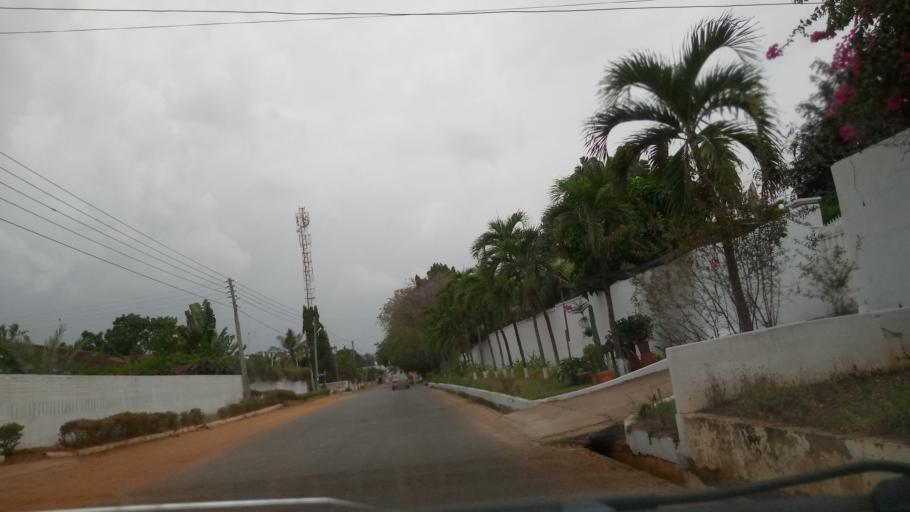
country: GH
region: Greater Accra
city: Accra
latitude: 5.6090
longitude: -0.1857
